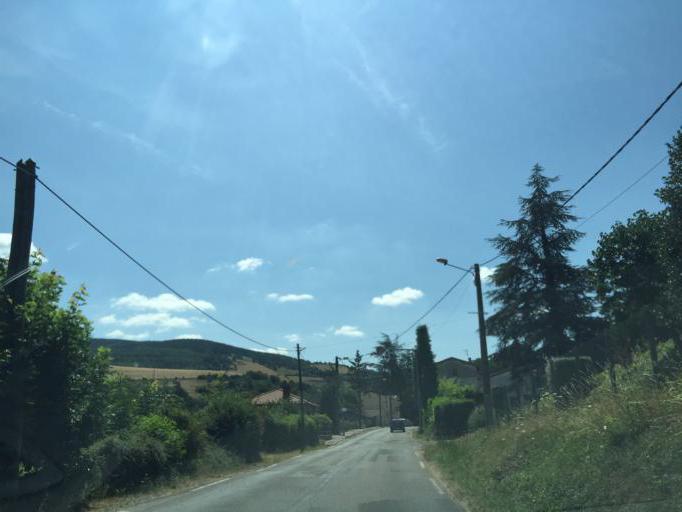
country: FR
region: Rhone-Alpes
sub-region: Departement de la Loire
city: Saint-Chamond
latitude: 45.4448
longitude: 4.5069
